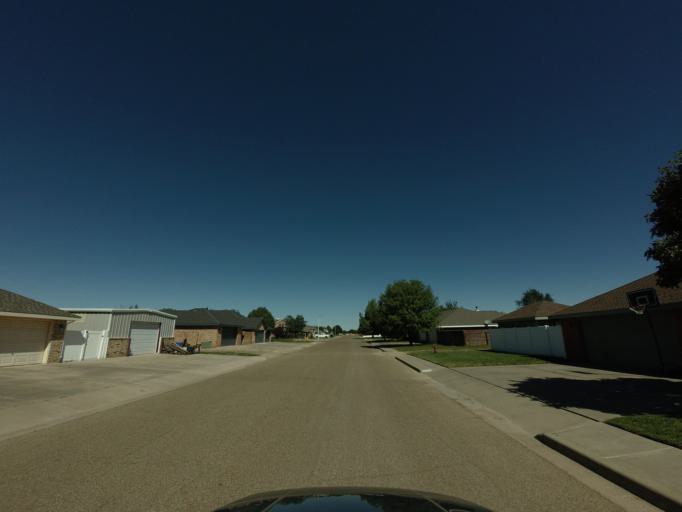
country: US
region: New Mexico
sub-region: Curry County
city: Clovis
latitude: 34.4291
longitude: -103.1721
